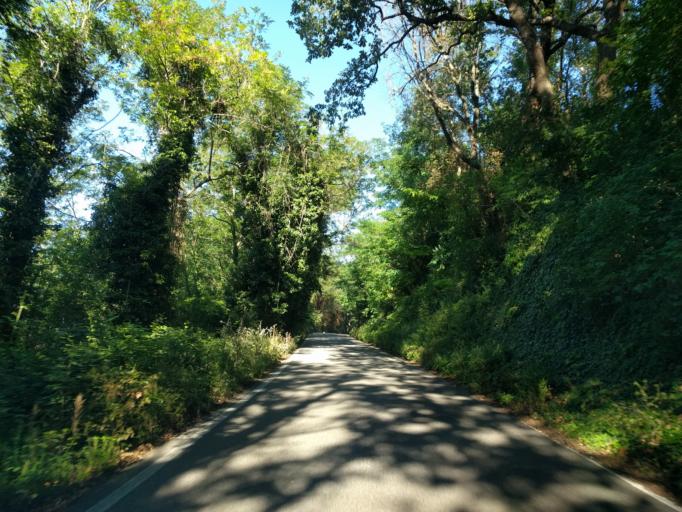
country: IT
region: The Marches
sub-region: Provincia di Pesaro e Urbino
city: Fenile
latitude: 43.8264
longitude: 12.9245
